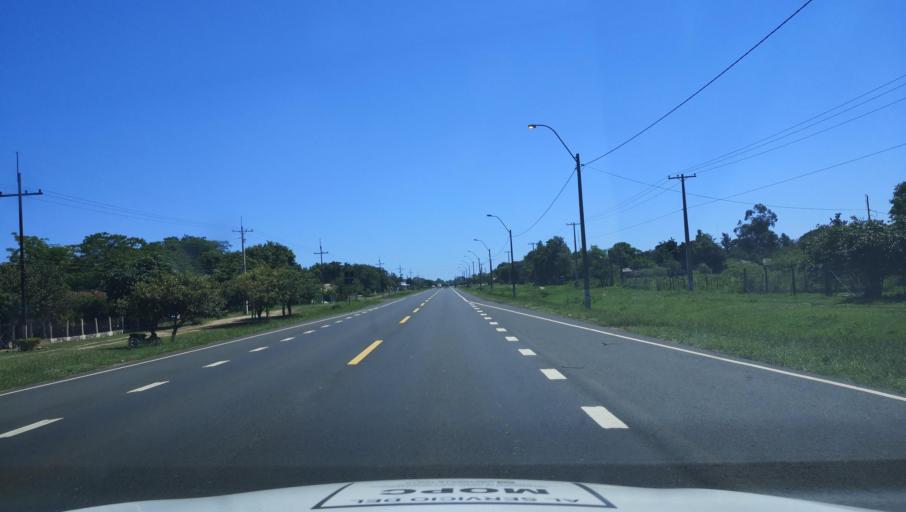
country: PY
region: Caaguazu
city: Carayao
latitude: -25.2079
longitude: -56.3986
